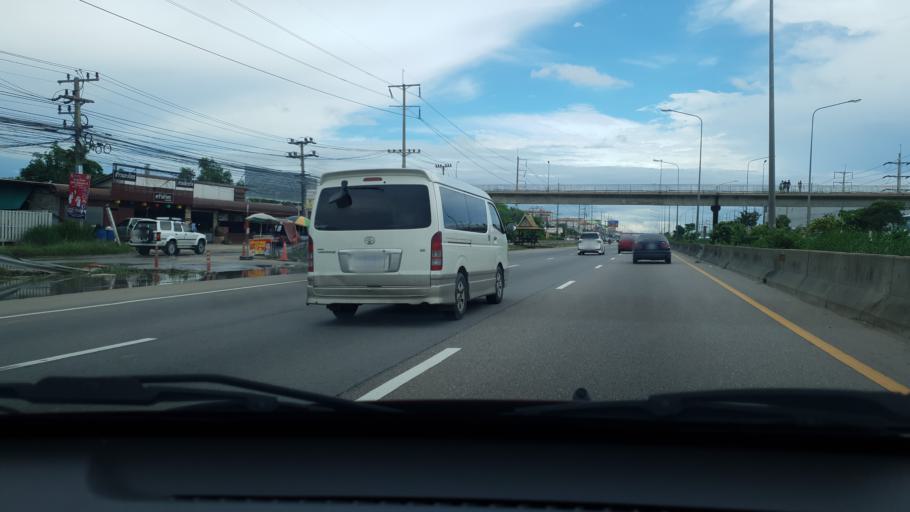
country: TH
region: Samut Sakhon
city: Ban Phaeo
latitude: 13.5118
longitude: 100.1442
